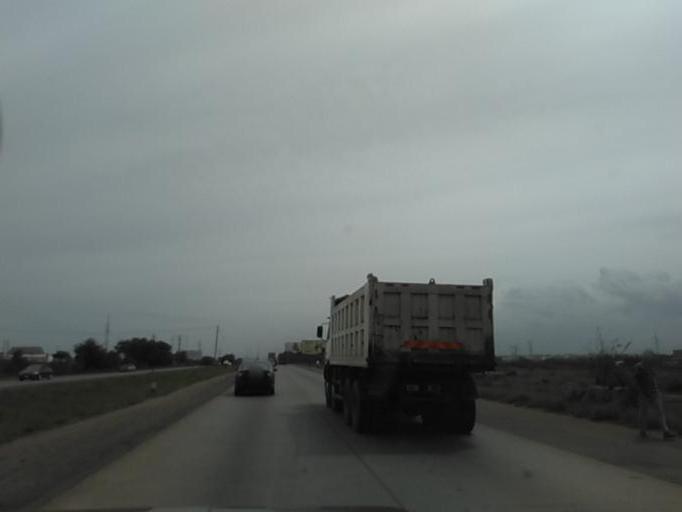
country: GH
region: Greater Accra
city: Tema
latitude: 5.6804
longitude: -0.0308
